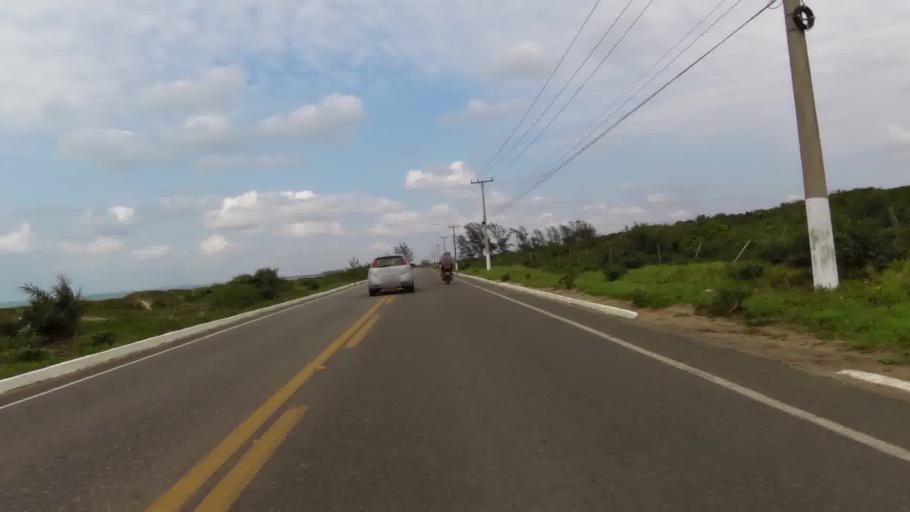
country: BR
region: Espirito Santo
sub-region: Piuma
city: Piuma
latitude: -20.9159
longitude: -40.7878
